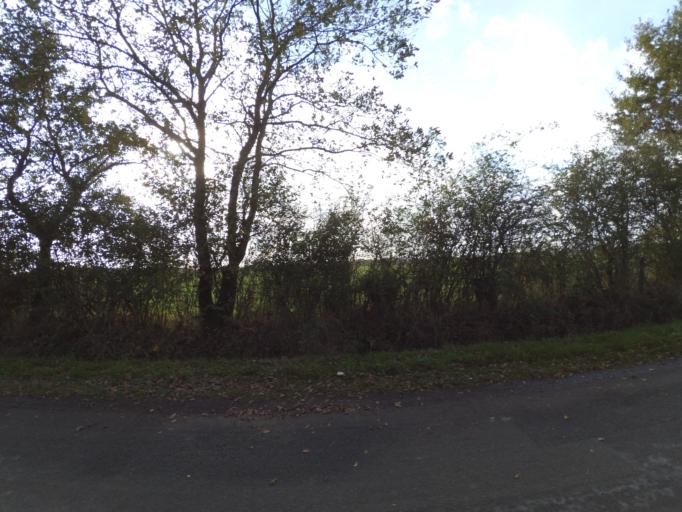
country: FR
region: Pays de la Loire
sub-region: Departement de la Vendee
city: Saint-Hilaire-de-Loulay
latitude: 47.0214
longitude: -1.3568
